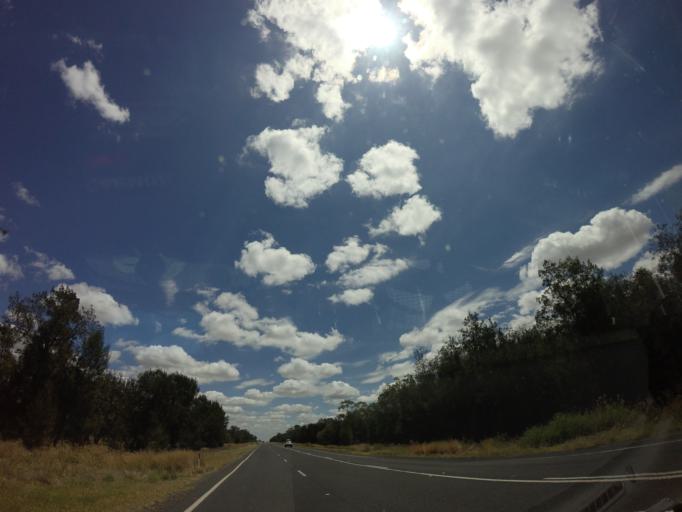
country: AU
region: New South Wales
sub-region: Moree Plains
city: Boggabilla
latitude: -28.9724
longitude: 150.0809
